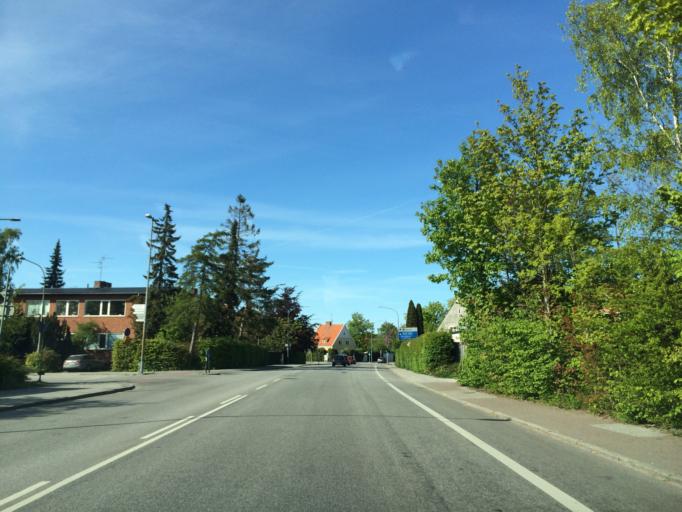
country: SE
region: Skane
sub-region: Lunds Kommun
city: Lund
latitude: 55.7056
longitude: 13.1771
